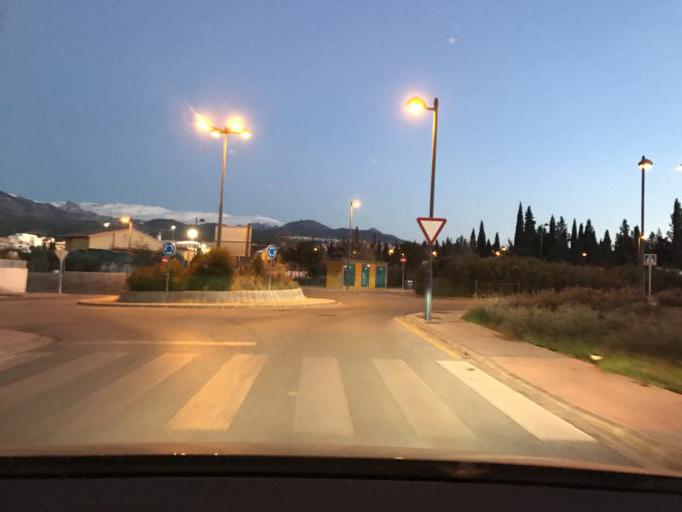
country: ES
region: Andalusia
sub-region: Provincia de Granada
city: Ogijares
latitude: 37.1164
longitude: -3.5972
